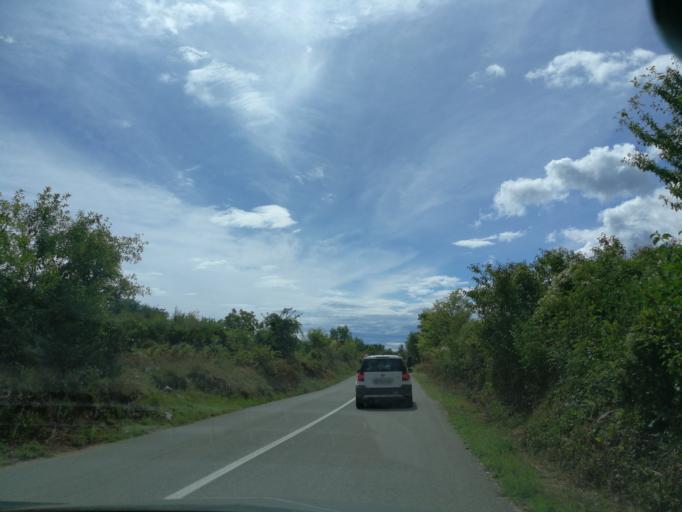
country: HR
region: Primorsko-Goranska
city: Punat
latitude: 45.1005
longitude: 14.6417
